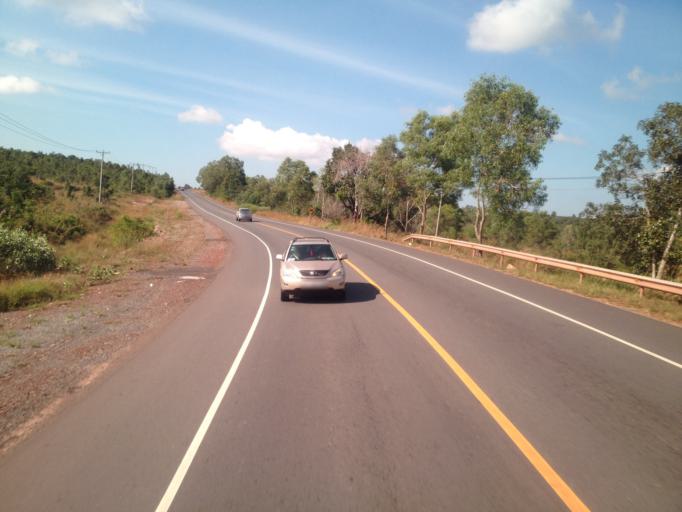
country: KH
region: Preah Sihanouk
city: Sihanoukville
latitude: 10.6063
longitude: 103.6135
